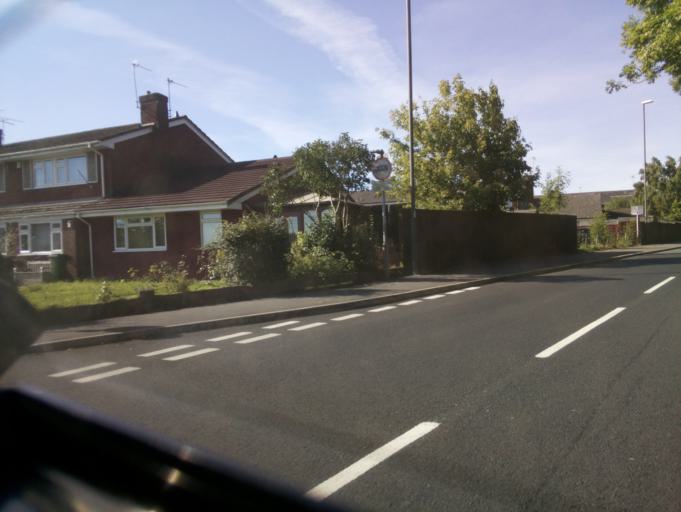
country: GB
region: England
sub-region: Bath and North East Somerset
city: Keynsham
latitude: 51.4069
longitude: -2.5153
